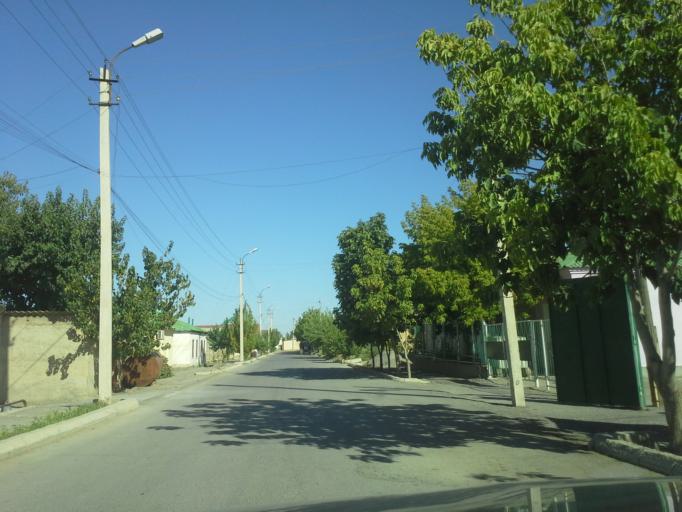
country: TM
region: Ahal
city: Abadan
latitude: 38.0713
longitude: 58.1544
